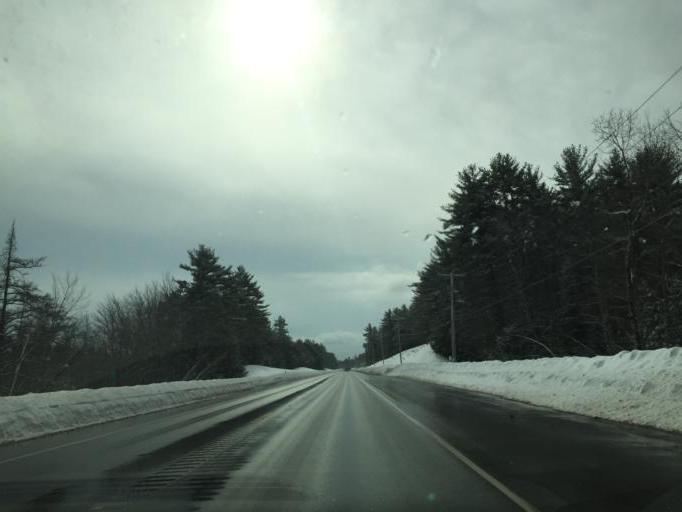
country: US
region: New Hampshire
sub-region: Carroll County
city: Sanbornville
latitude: 43.5373
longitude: -71.0312
